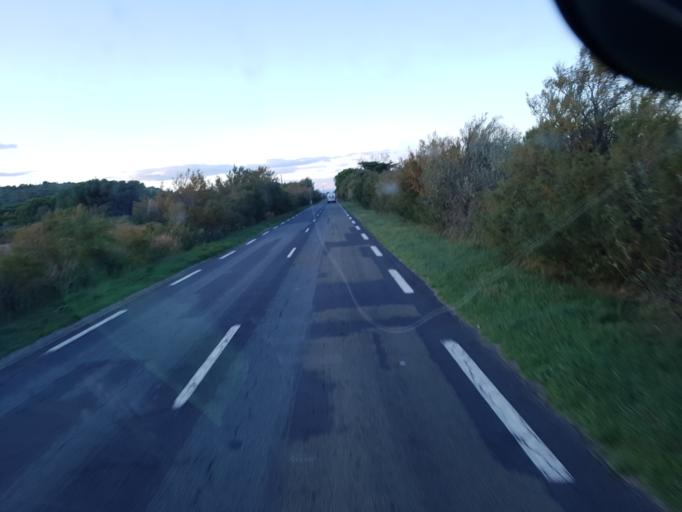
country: FR
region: Languedoc-Roussillon
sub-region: Departement de l'Aude
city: Port-la-Nouvelle
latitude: 43.0041
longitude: 3.0397
